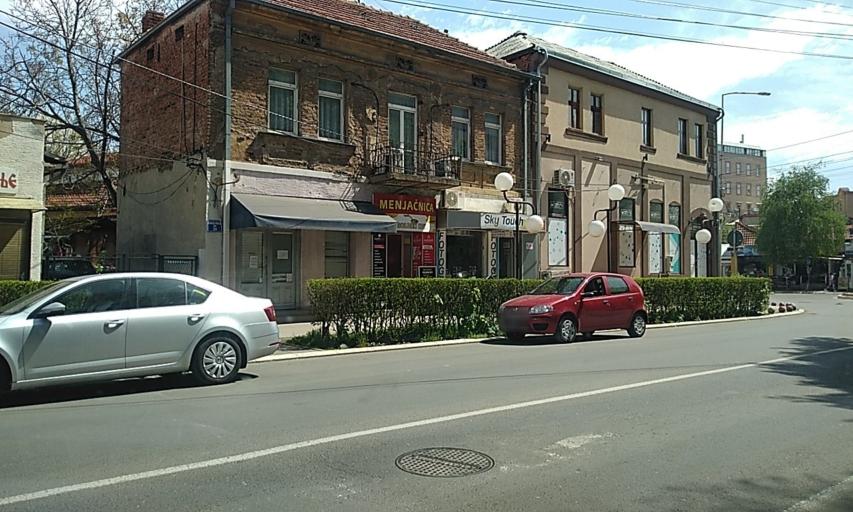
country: RS
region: Central Serbia
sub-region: Nisavski Okrug
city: Nis
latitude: 43.3188
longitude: 21.8994
